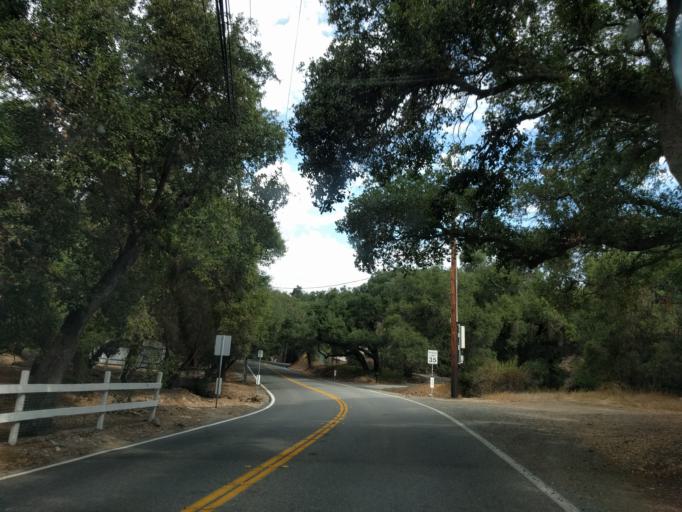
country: US
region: California
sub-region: Orange County
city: Trabuco Canyon
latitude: 33.6755
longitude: -117.6020
